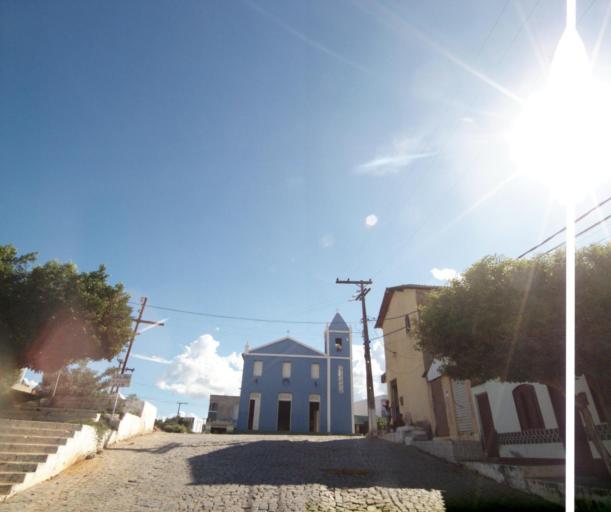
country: BR
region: Bahia
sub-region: Correntina
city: Correntina
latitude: -13.3440
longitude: -44.6364
